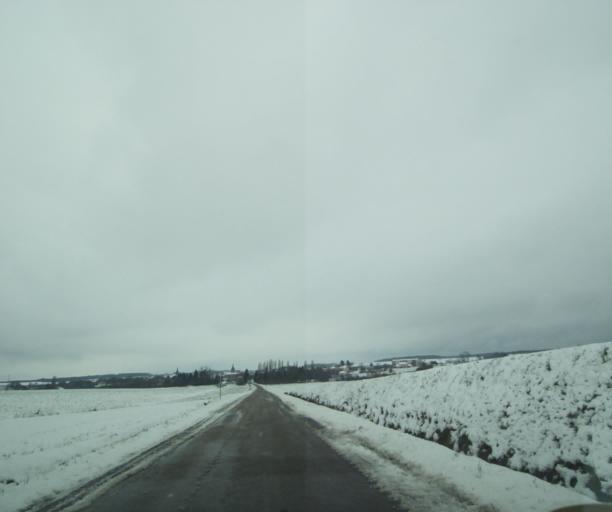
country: FR
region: Champagne-Ardenne
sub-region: Departement de la Haute-Marne
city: Laneuville-a-Remy
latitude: 48.4056
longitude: 4.8516
